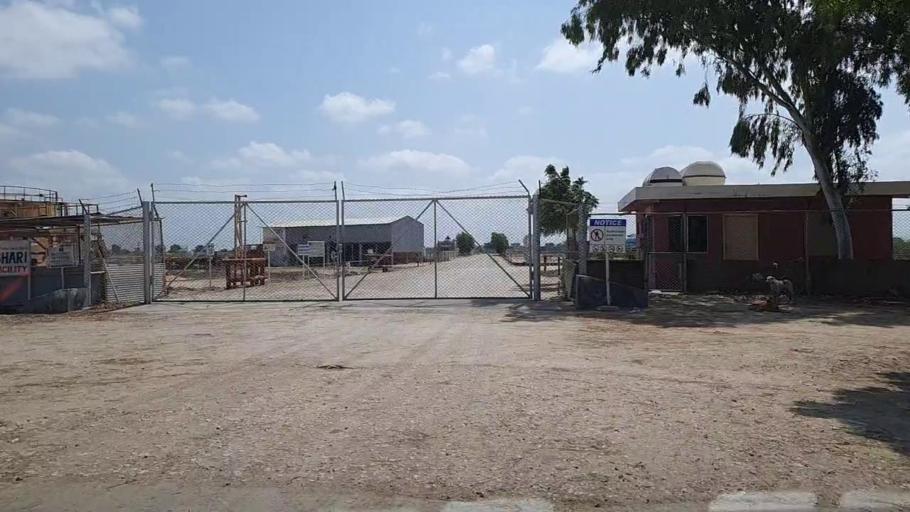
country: PK
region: Sindh
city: Talhar
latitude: 24.8790
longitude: 68.7201
